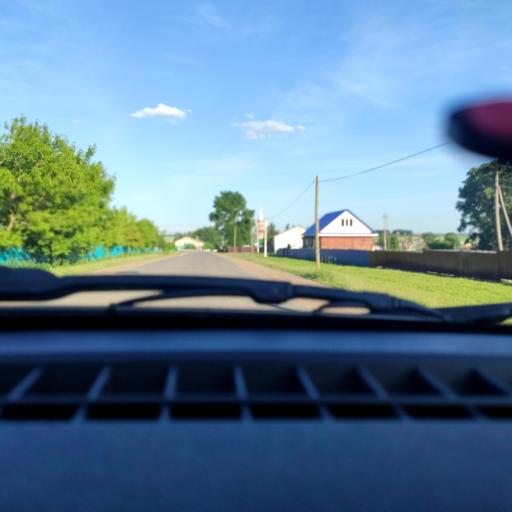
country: RU
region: Bashkortostan
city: Tolbazy
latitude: 54.2937
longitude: 55.8097
